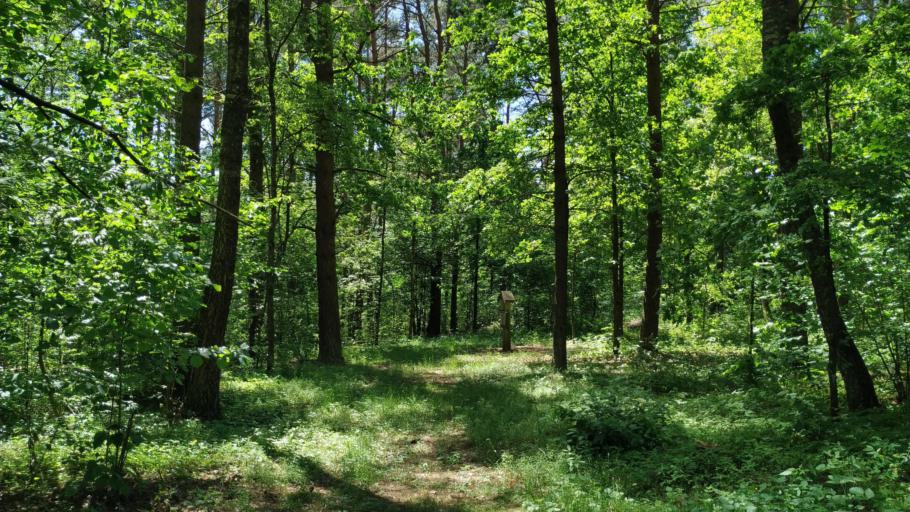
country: LT
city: Moletai
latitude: 55.0722
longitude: 25.2407
